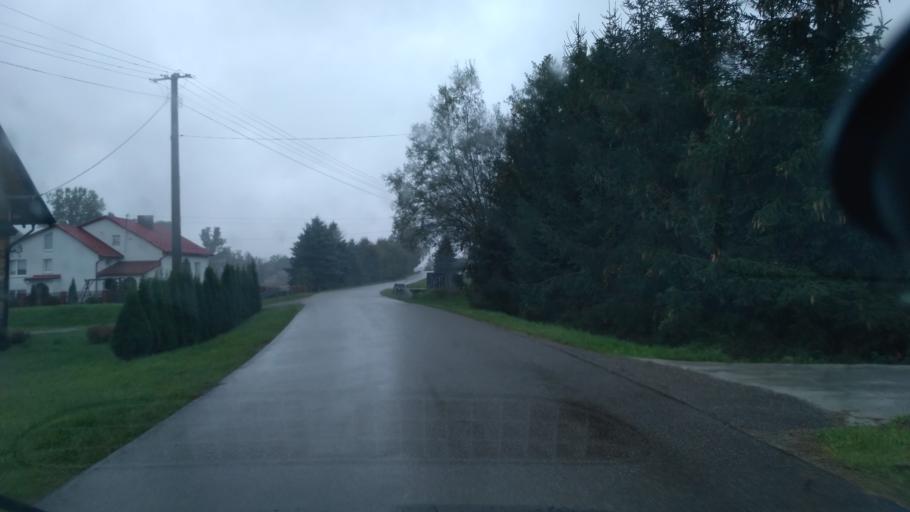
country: PL
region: Subcarpathian Voivodeship
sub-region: Powiat ropczycko-sedziszowski
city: Niedzwiada
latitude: 50.0018
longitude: 21.5505
